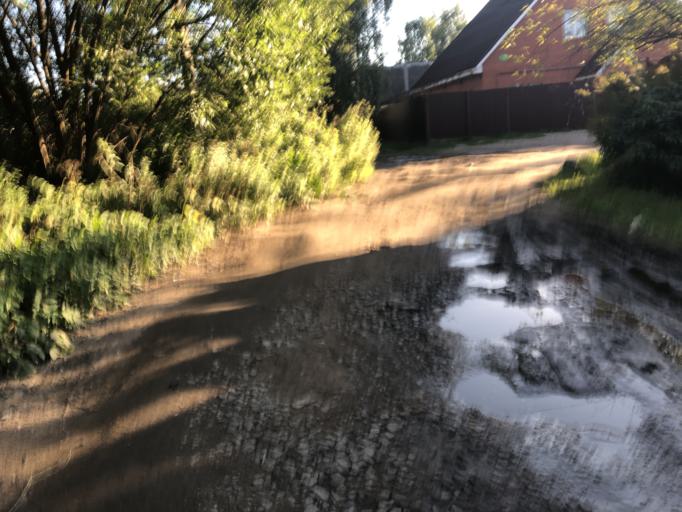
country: RU
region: Tverskaya
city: Rzhev
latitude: 56.2433
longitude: 34.3119
